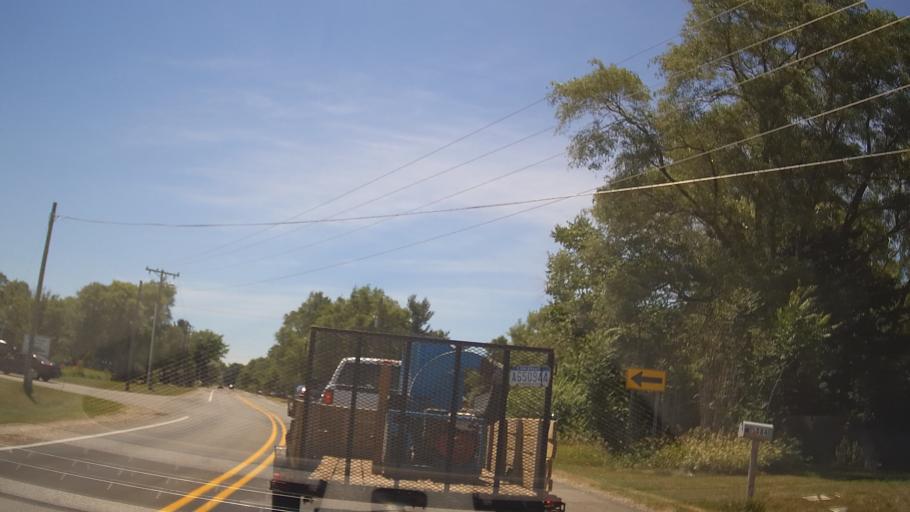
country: US
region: Michigan
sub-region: Grand Traverse County
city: Traverse City
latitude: 44.6637
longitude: -85.6919
